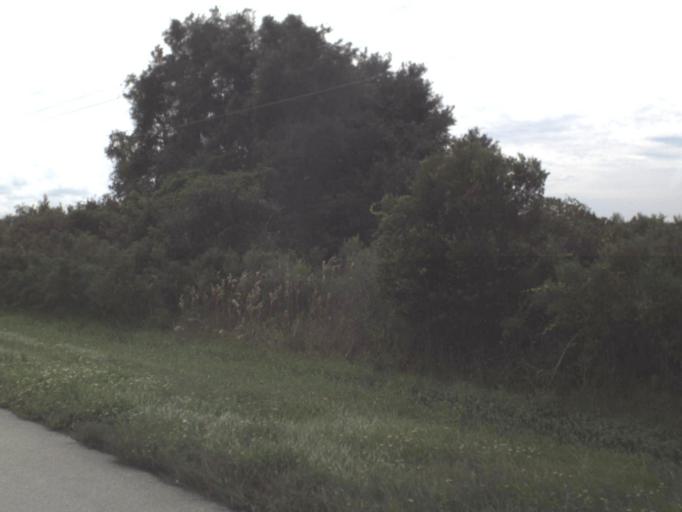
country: US
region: Florida
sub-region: DeSoto County
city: Southeast Arcadia
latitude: 27.1286
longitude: -81.7962
